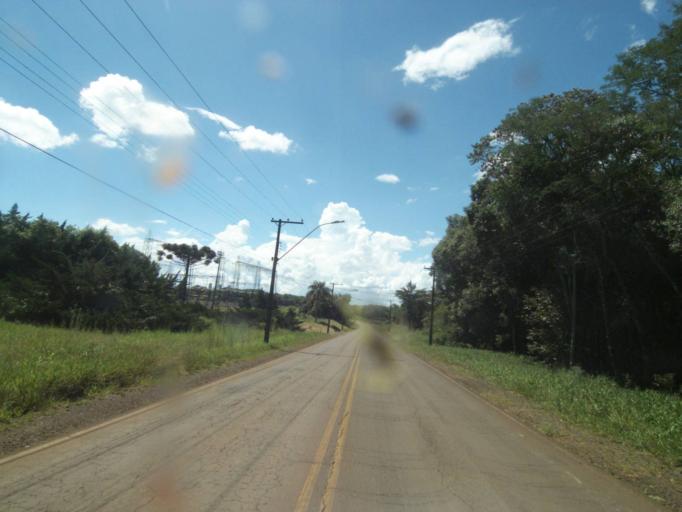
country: BR
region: Parana
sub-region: Chopinzinho
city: Chopinzinho
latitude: -25.7897
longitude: -52.0944
